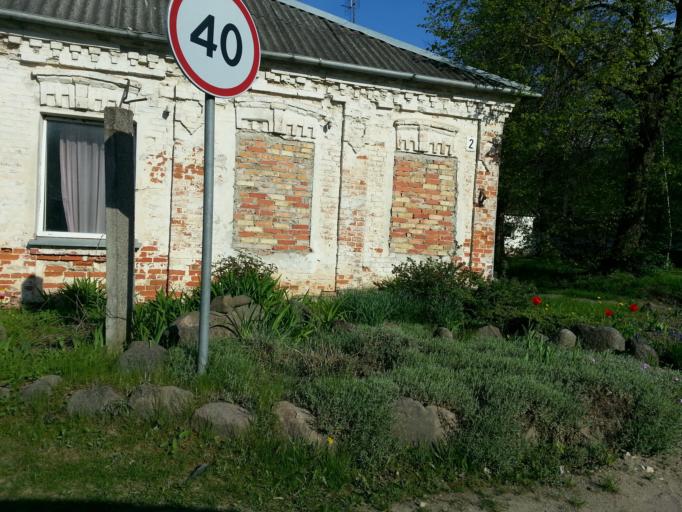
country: LT
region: Panevezys
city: Pasvalys
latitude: 55.9356
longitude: 24.3424
